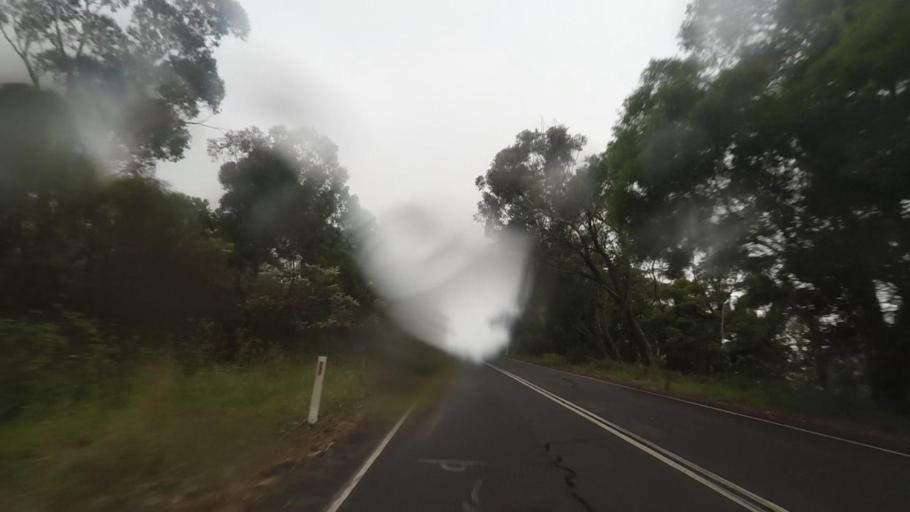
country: AU
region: New South Wales
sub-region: Wollongong
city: Mount Keira
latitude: -34.3994
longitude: 150.8422
